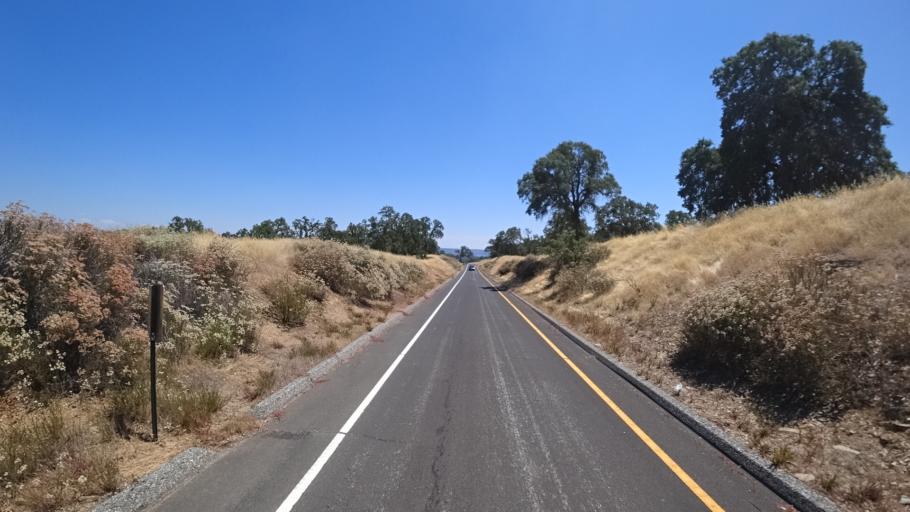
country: US
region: California
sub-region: Calaveras County
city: Angels Camp
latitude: 38.0191
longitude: -120.5269
